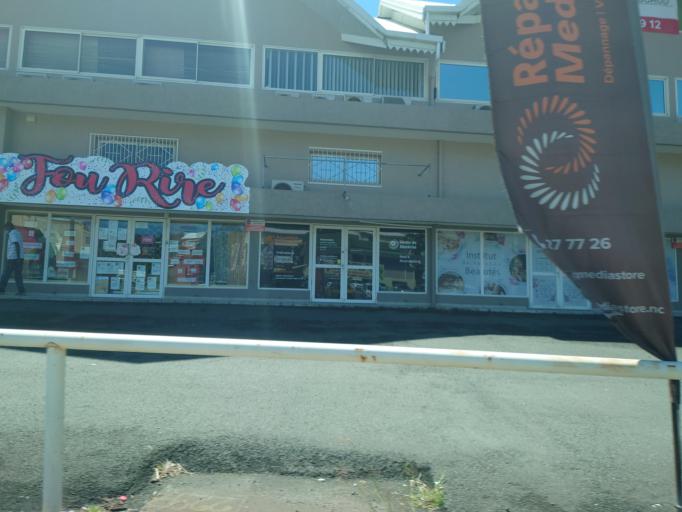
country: NC
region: South Province
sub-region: Noumea
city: Noumea
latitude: -22.2679
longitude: 166.4559
